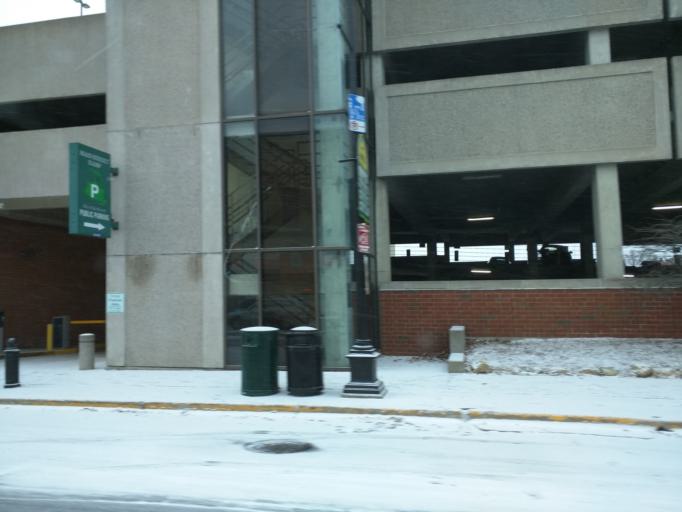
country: US
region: Wisconsin
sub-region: La Crosse County
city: La Crosse
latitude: 43.8133
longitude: -91.2523
